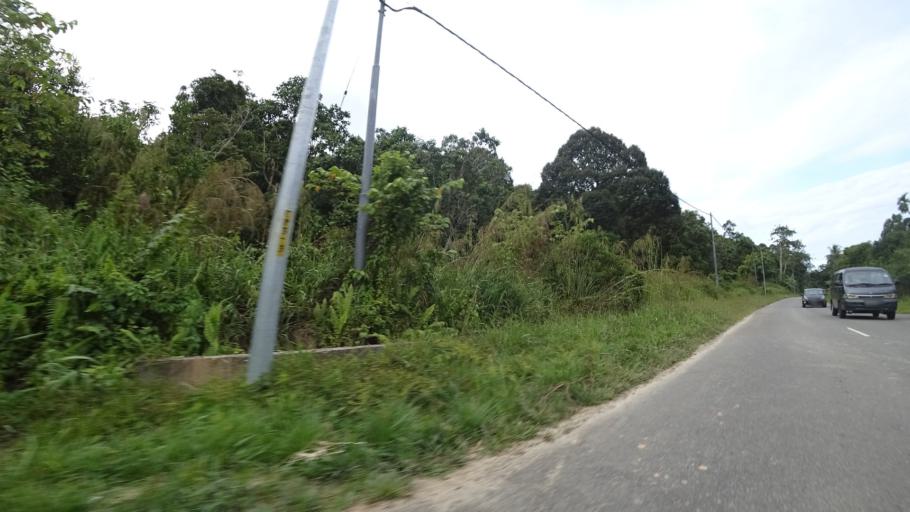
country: BN
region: Brunei and Muara
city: Bandar Seri Begawan
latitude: 4.8426
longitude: 114.9519
